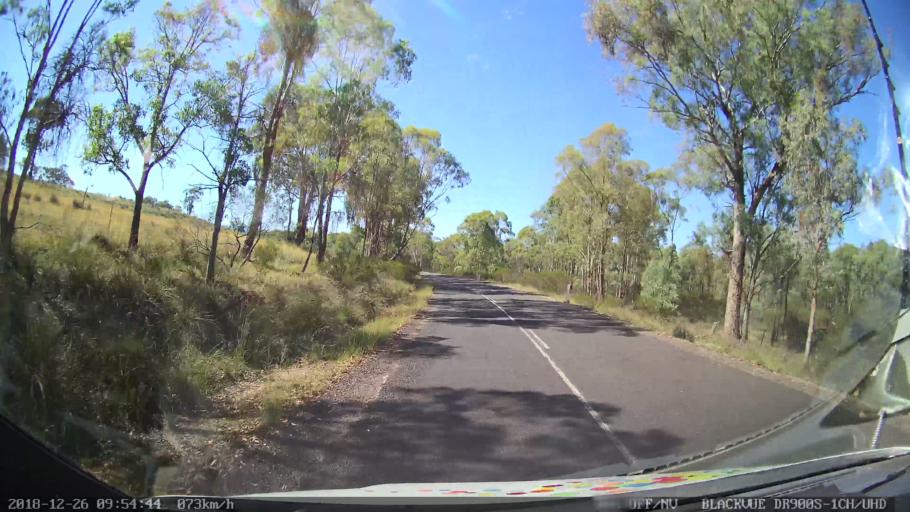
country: AU
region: New South Wales
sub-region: Mid-Western Regional
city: Kandos
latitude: -33.0331
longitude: 150.1617
